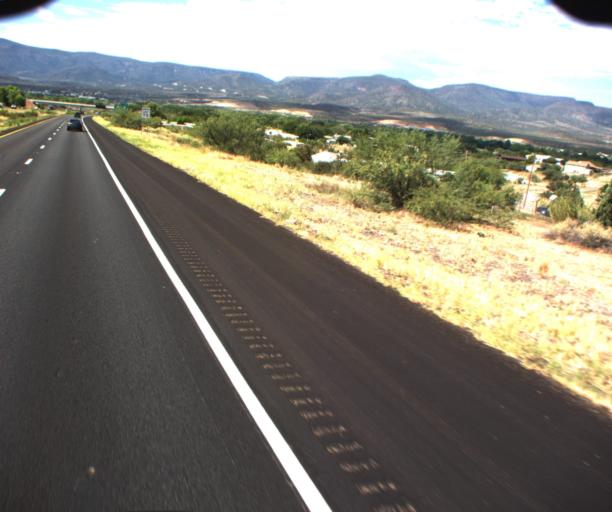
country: US
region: Arizona
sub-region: Yavapai County
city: Camp Verde
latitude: 34.6045
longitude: -111.8705
